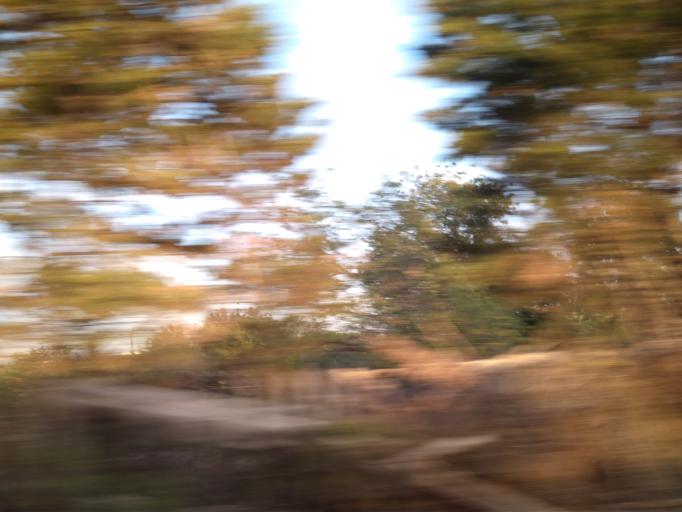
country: PT
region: Faro
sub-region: Faro
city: Santa Barbara de Nexe
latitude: 37.0618
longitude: -7.9549
